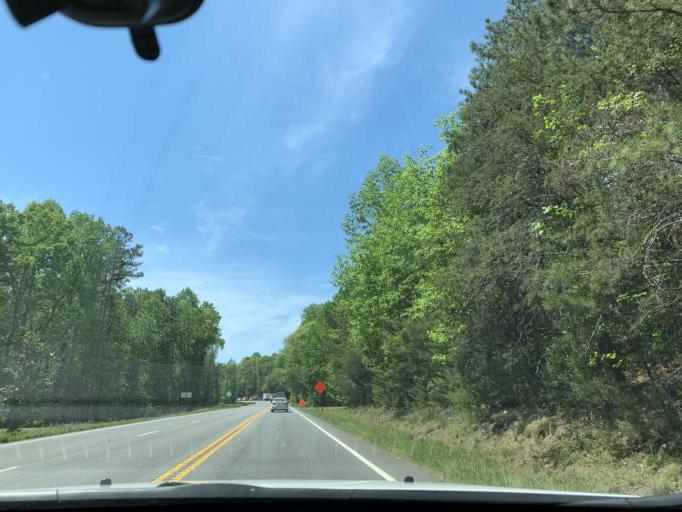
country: US
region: Georgia
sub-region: Forsyth County
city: Cumming
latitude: 34.2471
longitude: -84.0275
